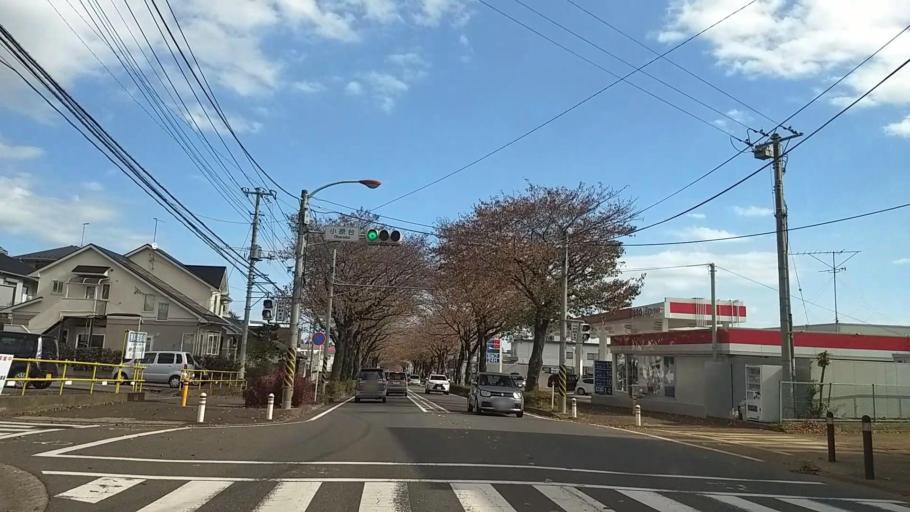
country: JP
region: Kanagawa
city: Hadano
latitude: 35.3621
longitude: 139.2242
